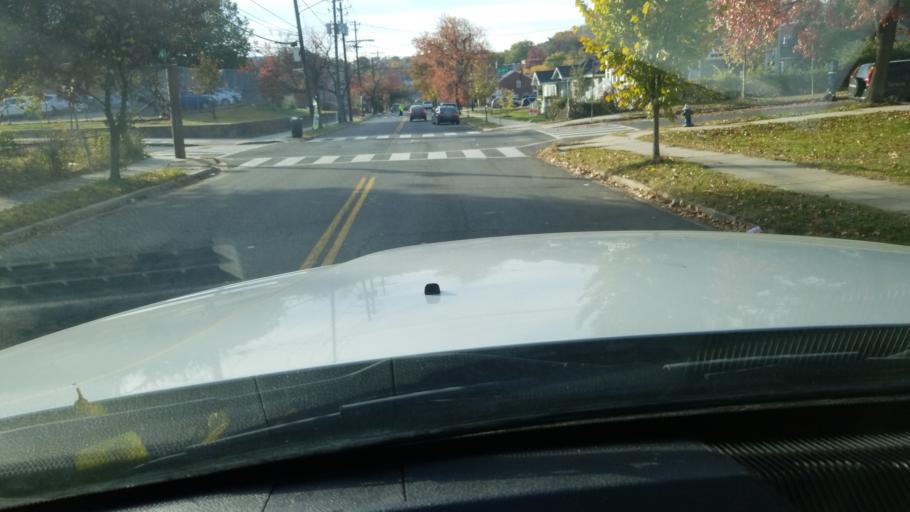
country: US
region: Maryland
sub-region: Prince George's County
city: Fairmount Heights
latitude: 38.8944
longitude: -76.9392
